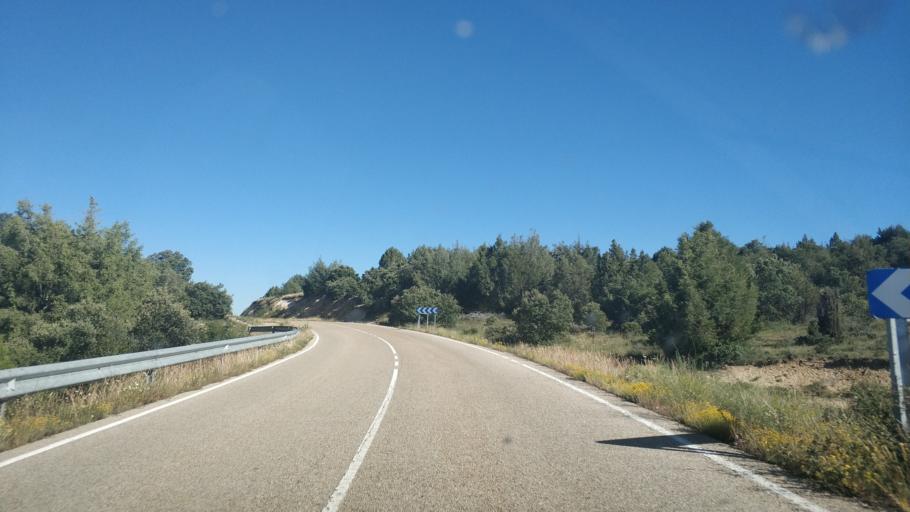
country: ES
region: Castille and Leon
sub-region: Provincia de Soria
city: Montejo de Tiermes
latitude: 41.4031
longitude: -3.2024
